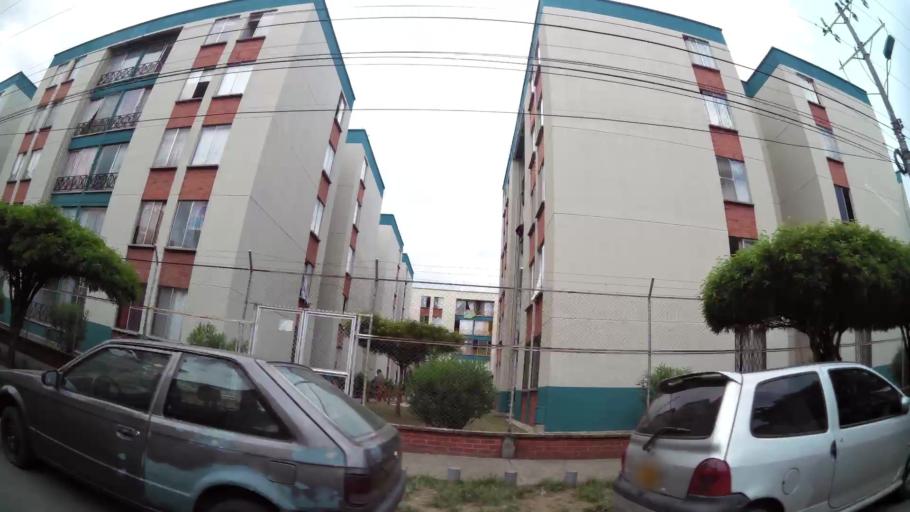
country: CO
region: Valle del Cauca
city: Cali
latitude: 3.4763
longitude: -76.4994
